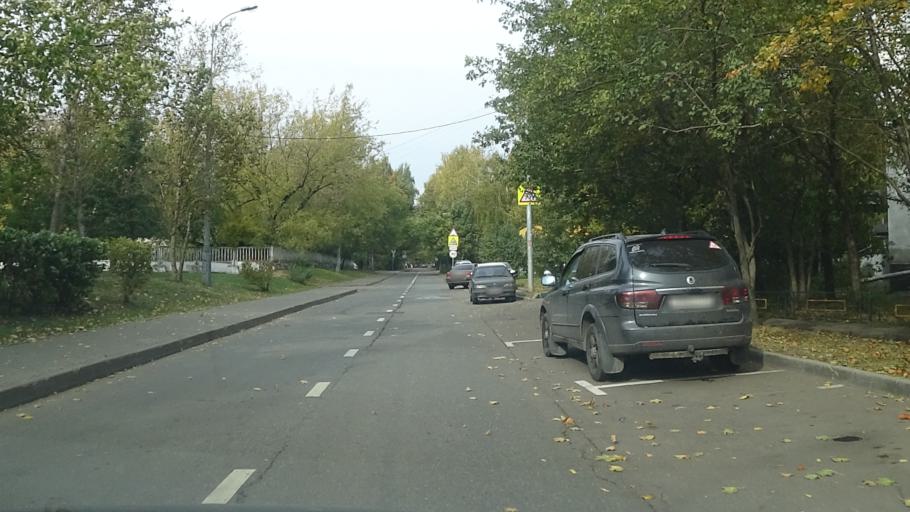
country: RU
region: Moscow
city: Solntsevo
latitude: 55.6562
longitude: 37.3915
